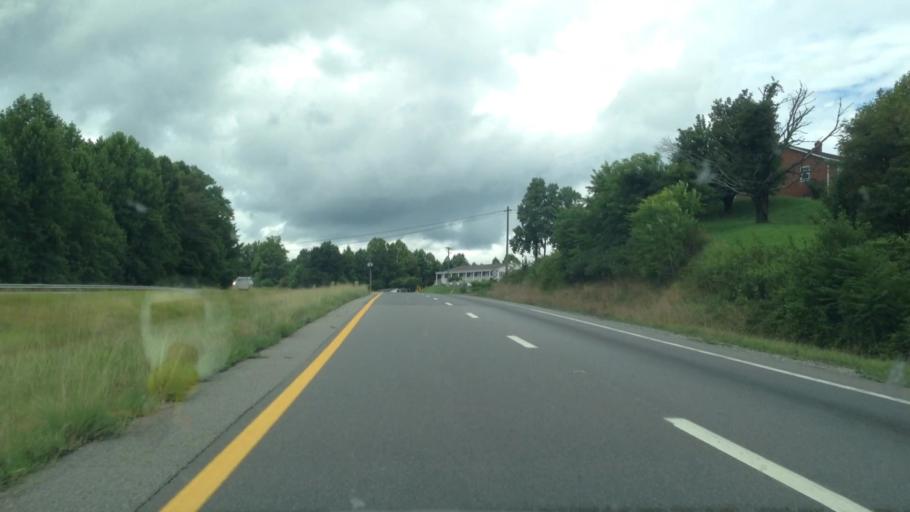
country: US
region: Virginia
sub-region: Henry County
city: Stanleytown
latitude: 36.7913
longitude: -79.9340
